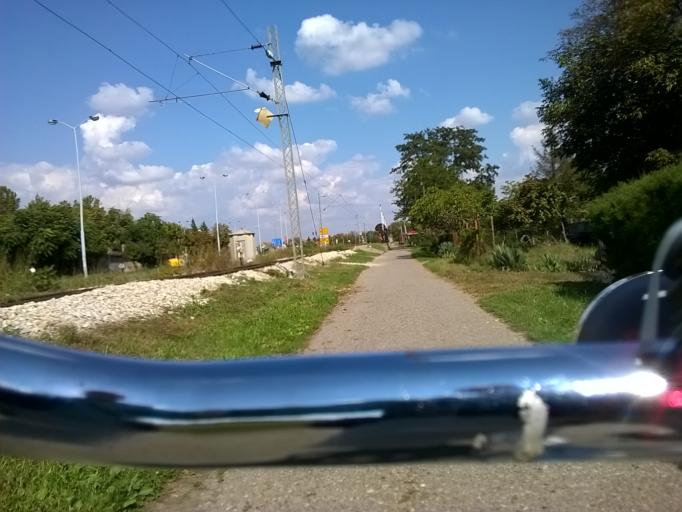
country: RS
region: Autonomna Pokrajina Vojvodina
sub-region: Juznobanatski Okrug
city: Pancevo
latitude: 44.8691
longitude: 20.6652
